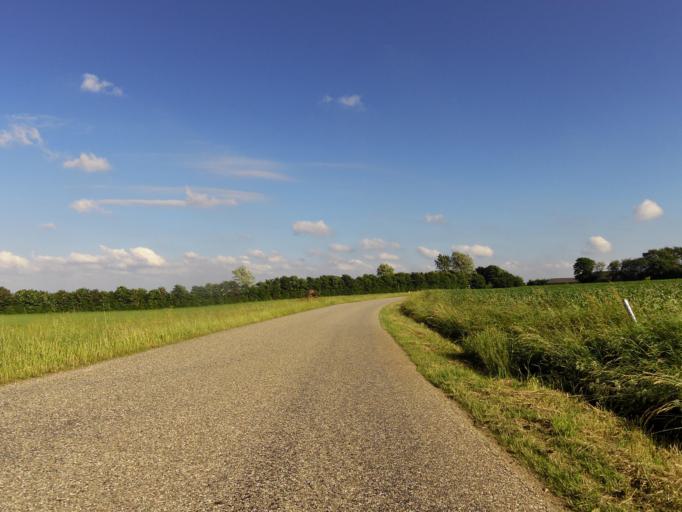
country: DK
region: South Denmark
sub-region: Vejen Kommune
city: Rodding
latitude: 55.3252
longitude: 9.1791
